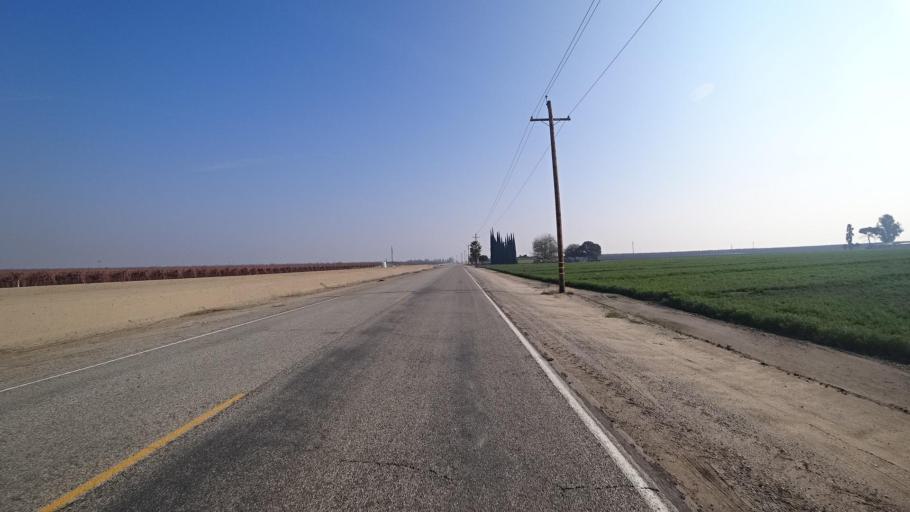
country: US
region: California
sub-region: Kern County
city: Buttonwillow
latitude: 35.3546
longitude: -119.3860
